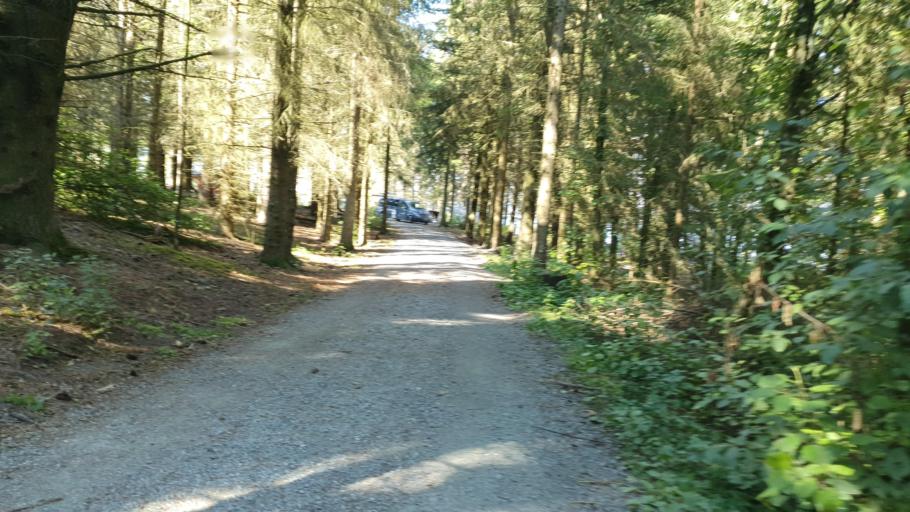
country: NO
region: Nord-Trondelag
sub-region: Levanger
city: Levanger
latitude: 63.7794
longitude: 11.3876
